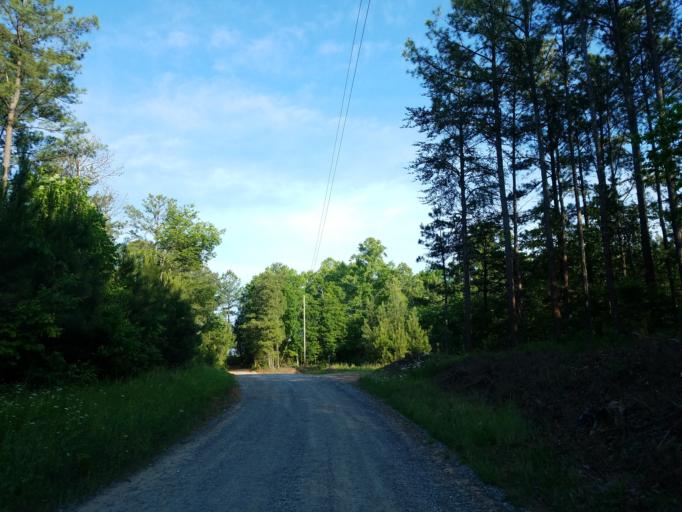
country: US
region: Georgia
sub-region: Pickens County
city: Nelson
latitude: 34.3659
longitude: -84.3255
